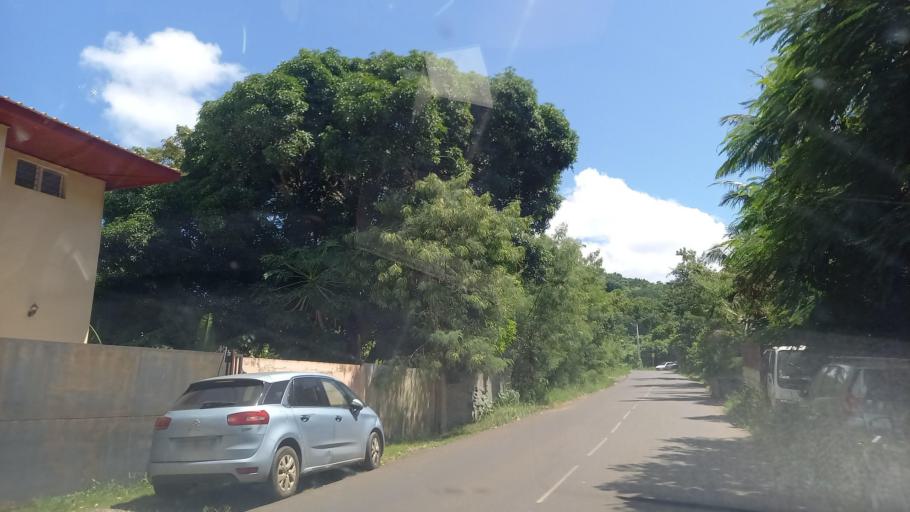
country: YT
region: Kani-Keli
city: Kani Keli
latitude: -12.9234
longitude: 45.1020
